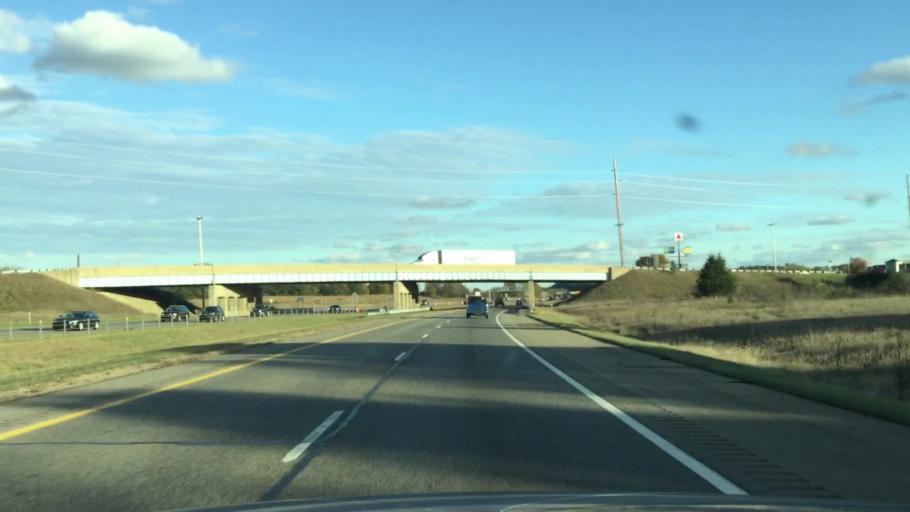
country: US
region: Michigan
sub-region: Calhoun County
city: Marshall
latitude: 42.2949
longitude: -84.9663
